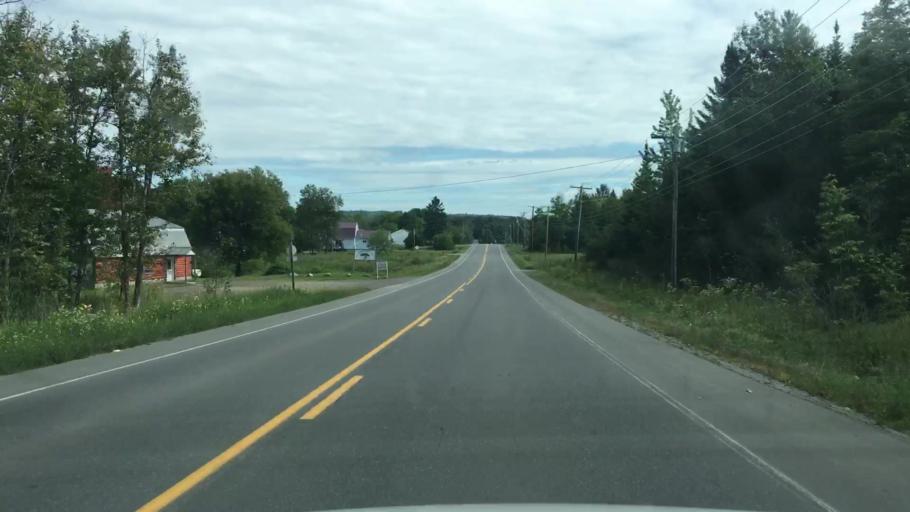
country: US
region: Maine
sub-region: Piscataquis County
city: Dover-Foxcroft
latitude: 45.1950
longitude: -69.2144
